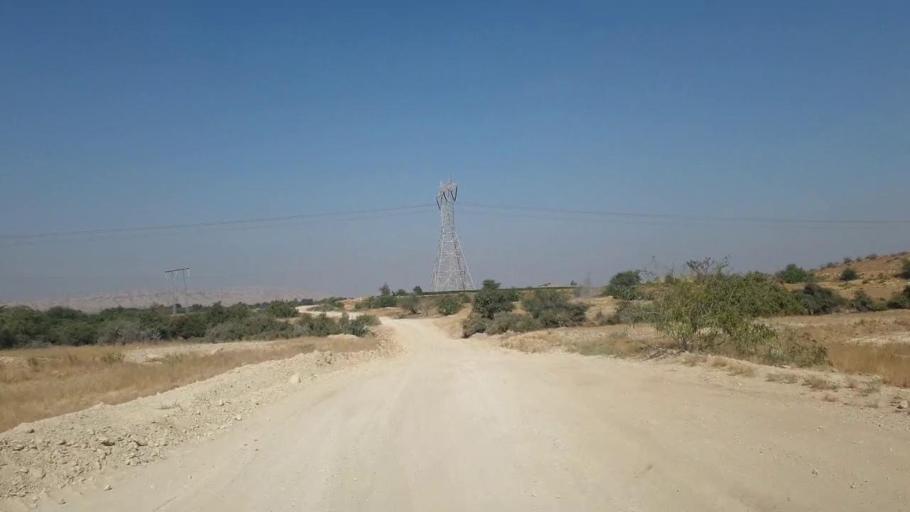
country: PK
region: Sindh
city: Thatta
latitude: 25.2436
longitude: 67.8044
